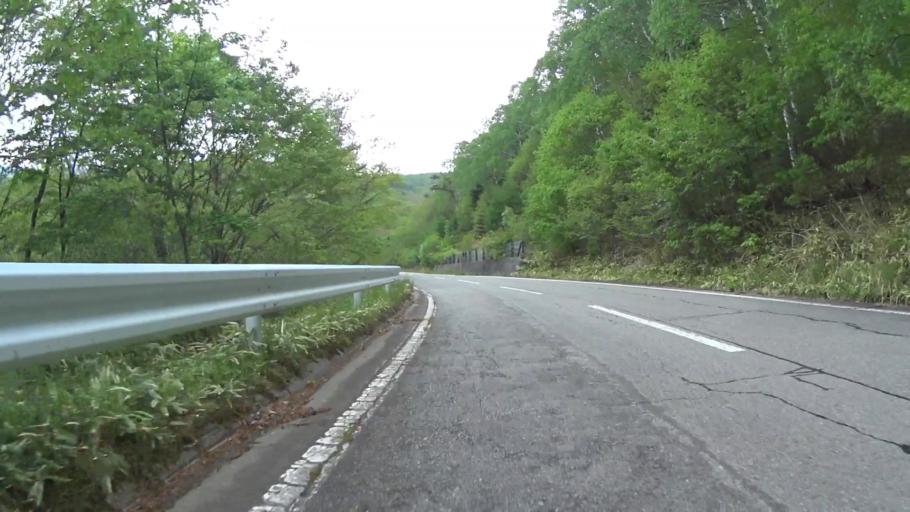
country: JP
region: Nagano
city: Saku
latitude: 36.0836
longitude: 138.3847
